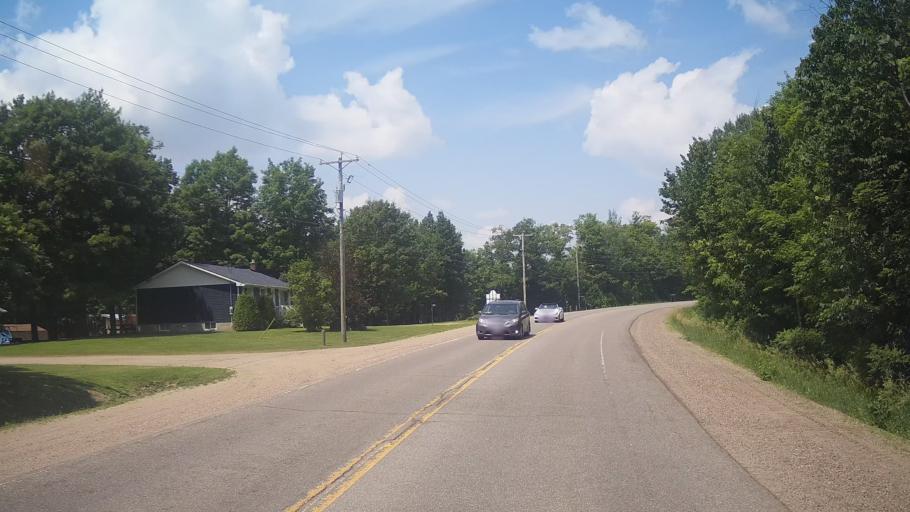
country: CA
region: Quebec
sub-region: Outaouais
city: Shawville
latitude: 45.5747
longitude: -76.4458
